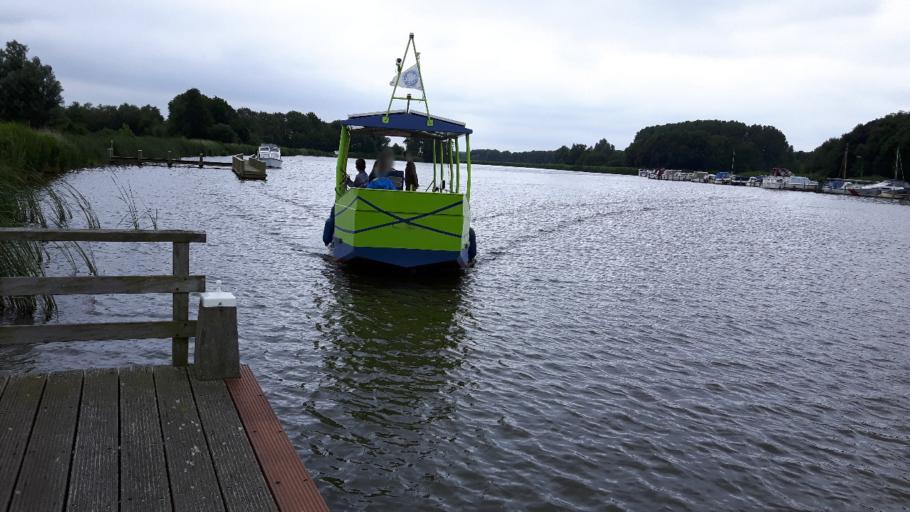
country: NL
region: South Holland
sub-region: Gemeente Lansingerland
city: Bleiswijk
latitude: 52.0146
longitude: 4.5579
